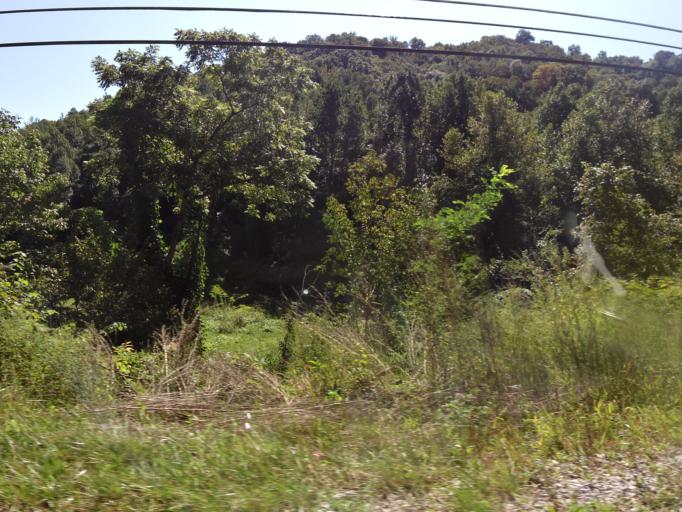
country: US
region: Kentucky
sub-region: Clay County
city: Manchester
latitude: 37.1535
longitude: -83.5938
